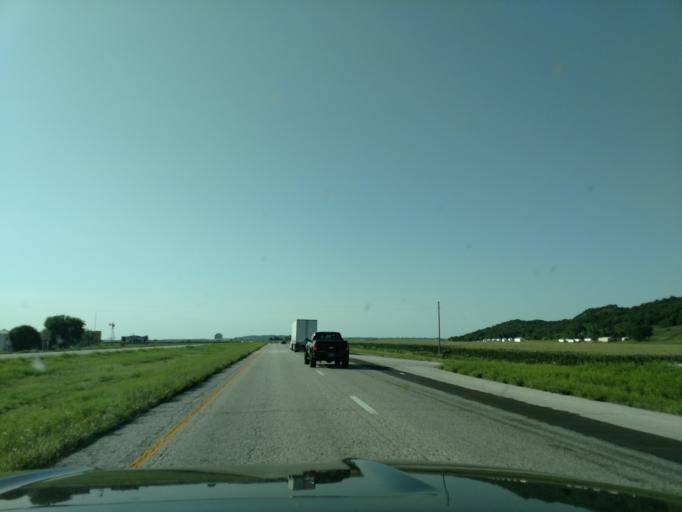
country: US
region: Missouri
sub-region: Atchison County
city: Rock Port
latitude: 40.4789
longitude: -95.5932
